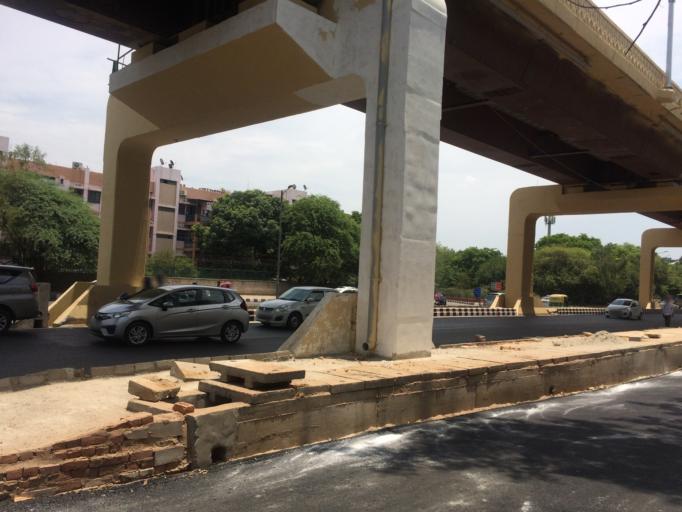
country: IN
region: NCT
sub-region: Central Delhi
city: Karol Bagh
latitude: 28.5696
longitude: 77.1635
